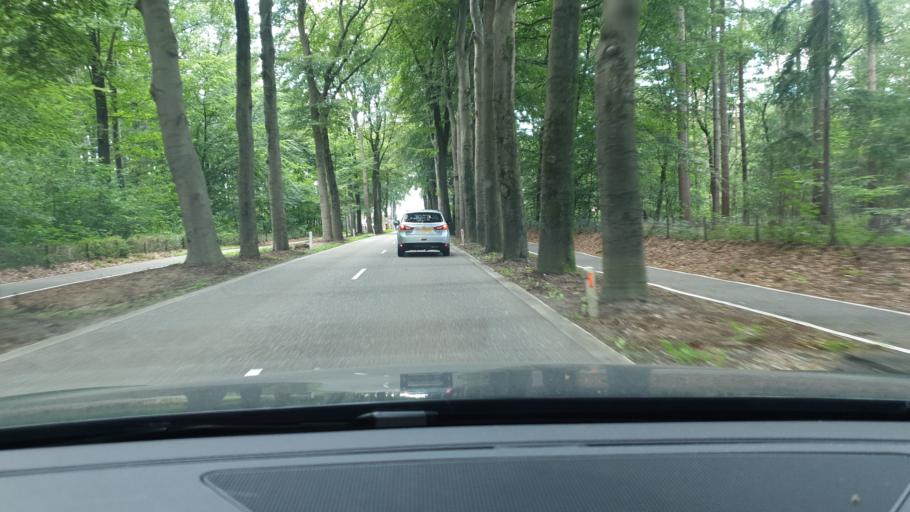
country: NL
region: Gelderland
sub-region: Gemeente Groesbeek
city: Groesbeek
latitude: 51.7657
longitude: 5.9099
